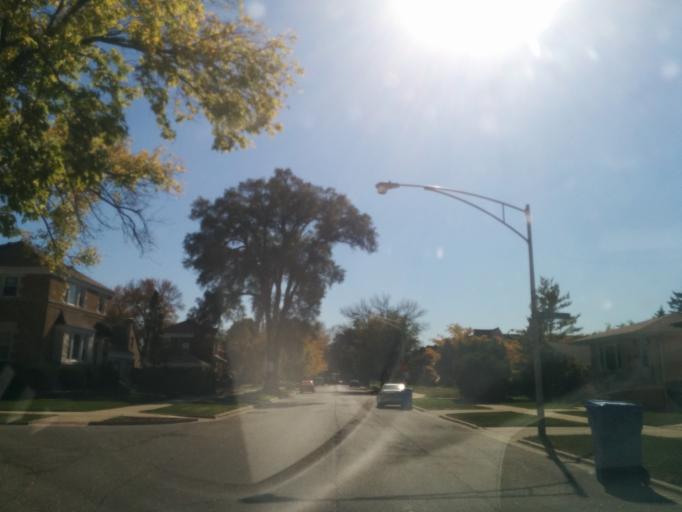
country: US
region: Illinois
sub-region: Cook County
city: Elmwood Park
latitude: 41.9407
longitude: -87.7921
